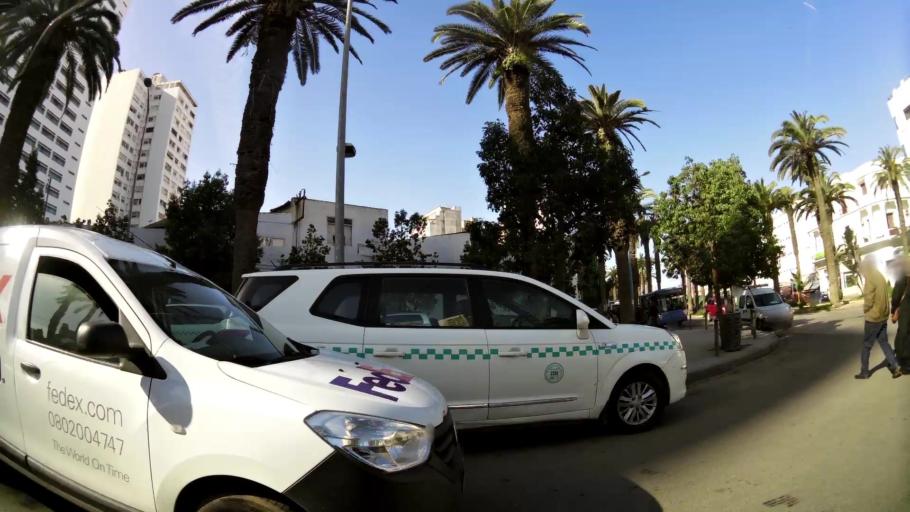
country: MA
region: Grand Casablanca
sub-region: Casablanca
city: Casablanca
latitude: 33.5988
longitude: -7.6143
